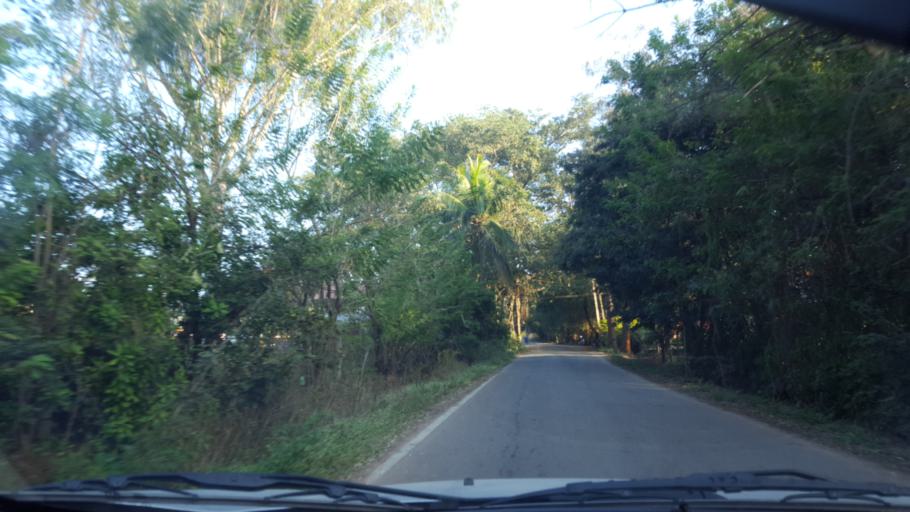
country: IN
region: Karnataka
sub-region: Bangalore Urban
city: Yelahanka
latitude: 13.1749
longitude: 77.5943
